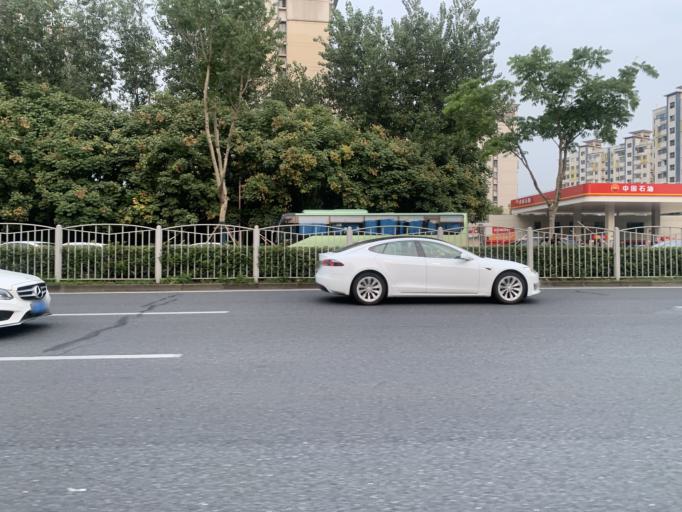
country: CN
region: Shanghai Shi
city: Huamu
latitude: 31.1922
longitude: 121.5203
